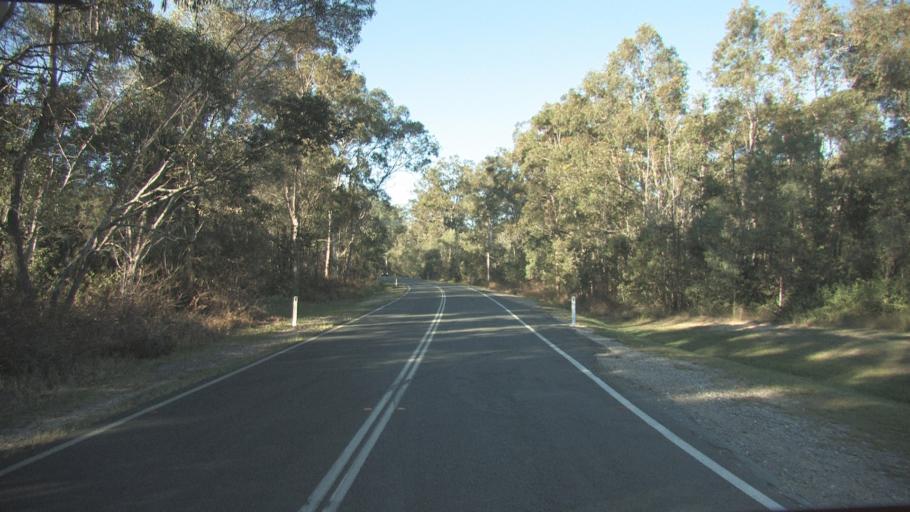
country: AU
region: Queensland
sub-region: Logan
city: Chambers Flat
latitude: -27.7794
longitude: 153.0712
